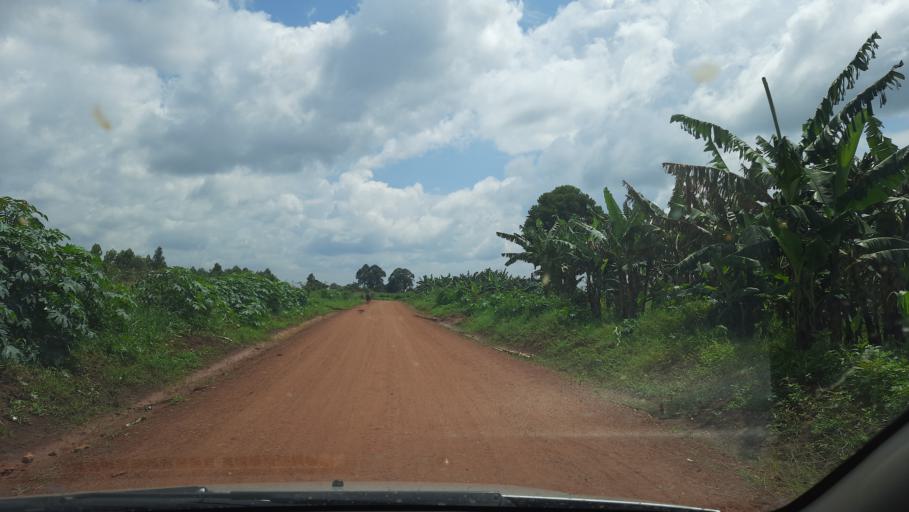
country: UG
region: Western Region
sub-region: Kiryandongo District
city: Kiryandongo
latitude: 1.8203
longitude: 31.9845
